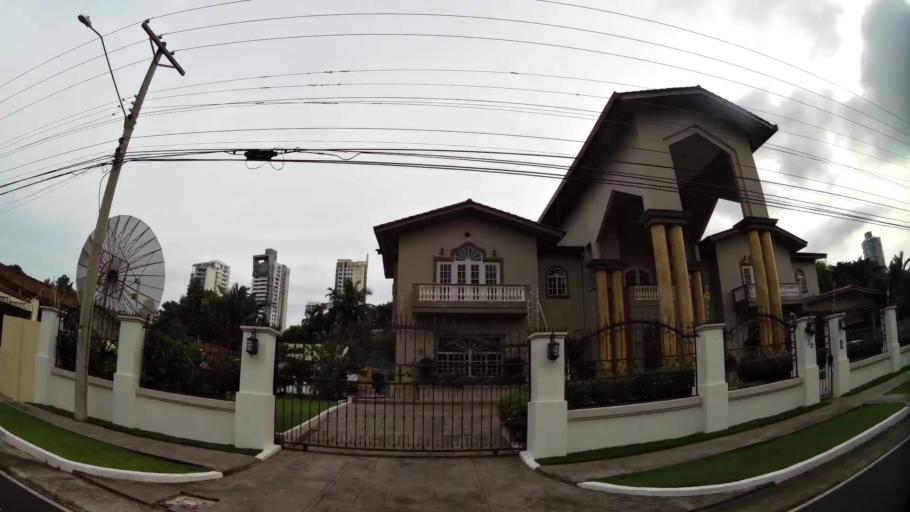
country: PA
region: Panama
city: Panama
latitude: 8.9996
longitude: -79.4996
